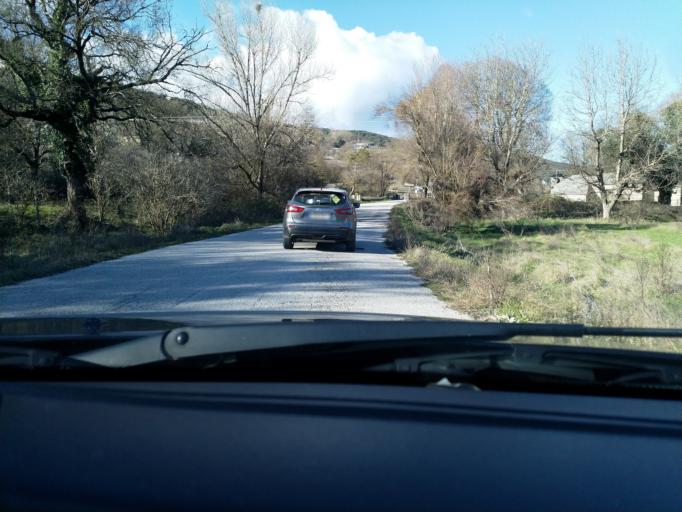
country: GR
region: Epirus
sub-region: Nomos Ioanninon
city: Kalpaki
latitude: 39.8789
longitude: 20.6794
